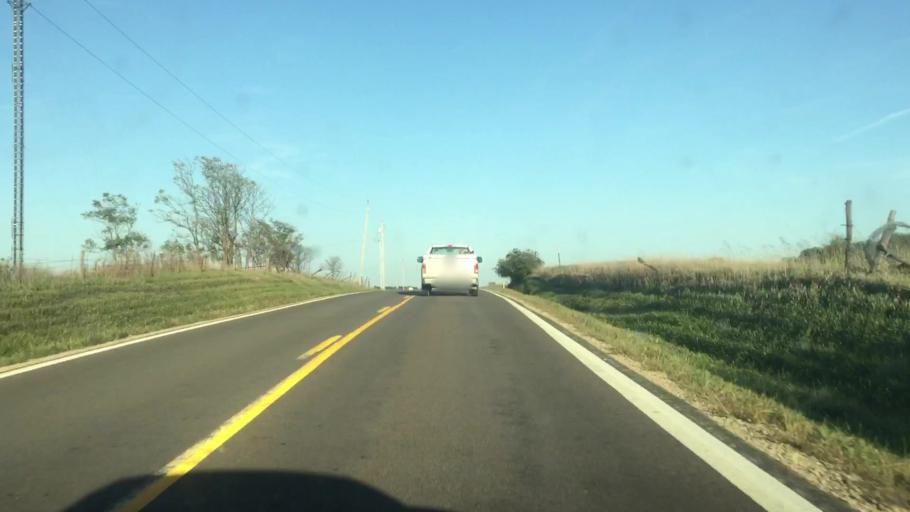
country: US
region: Kansas
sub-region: Brown County
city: Horton
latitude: 39.5513
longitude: -95.4250
